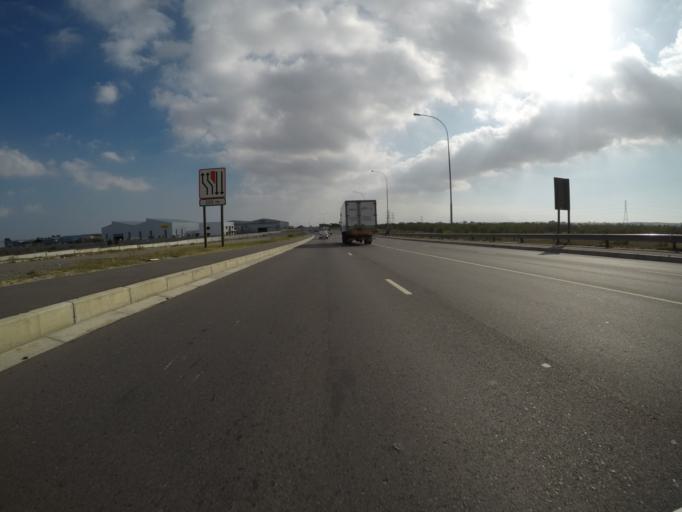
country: ZA
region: Western Cape
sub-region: City of Cape Town
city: Kraaifontein
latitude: -33.9541
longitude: 18.6911
